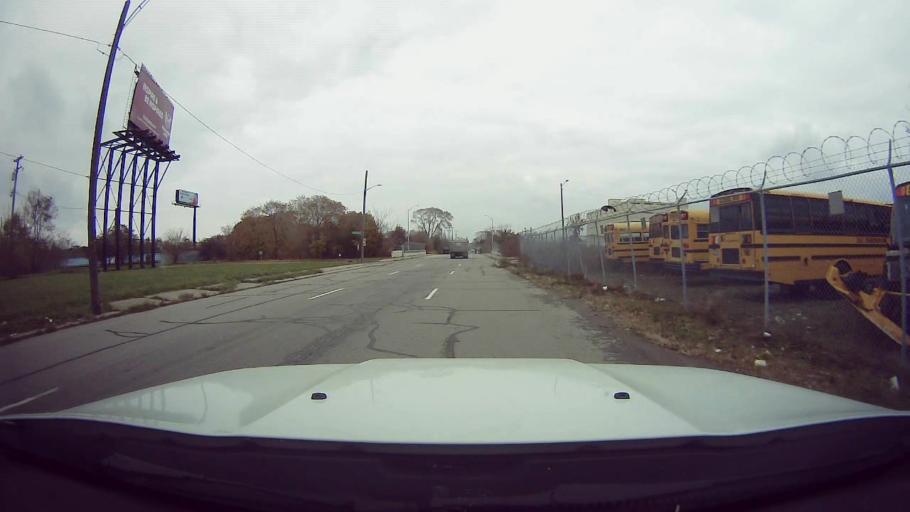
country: US
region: Michigan
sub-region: Wayne County
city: Detroit
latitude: 42.3538
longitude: -83.0846
